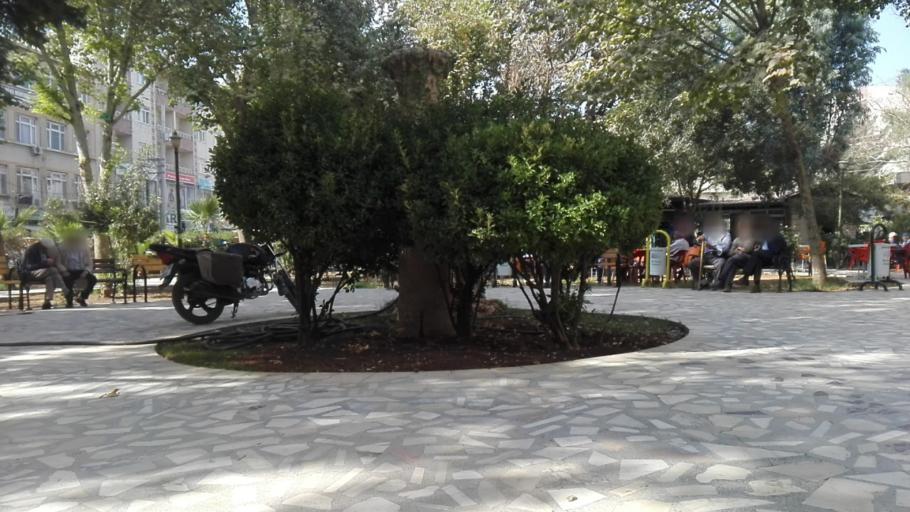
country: TR
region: Mardin
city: Nusaybin
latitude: 37.0699
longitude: 41.2149
